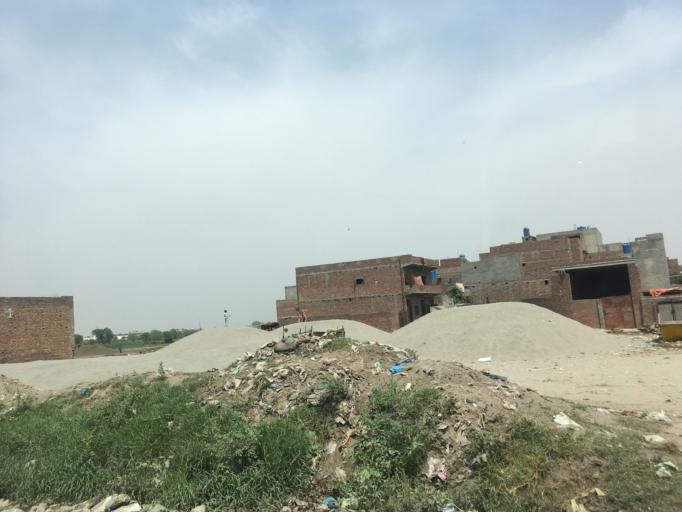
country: PK
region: Punjab
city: Lahore
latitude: 31.6122
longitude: 74.3275
